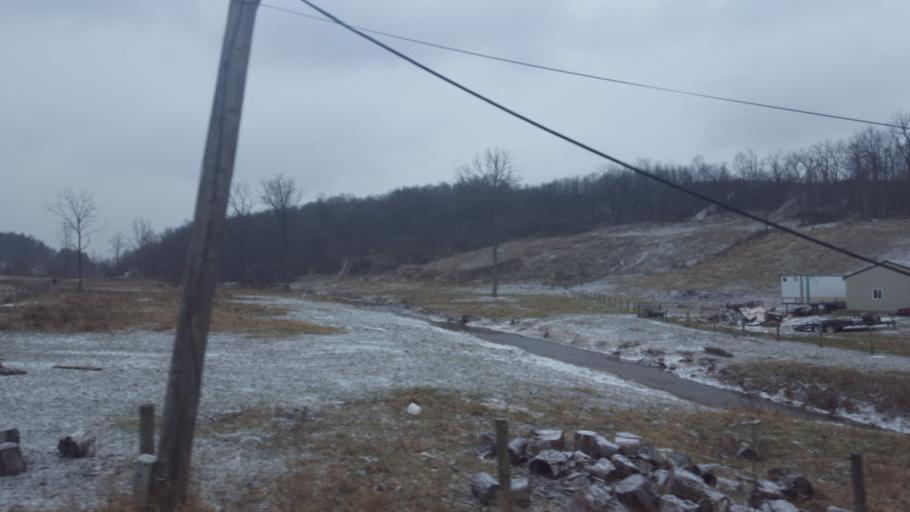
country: US
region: Ohio
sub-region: Coshocton County
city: West Lafayette
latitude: 40.3870
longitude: -81.7576
